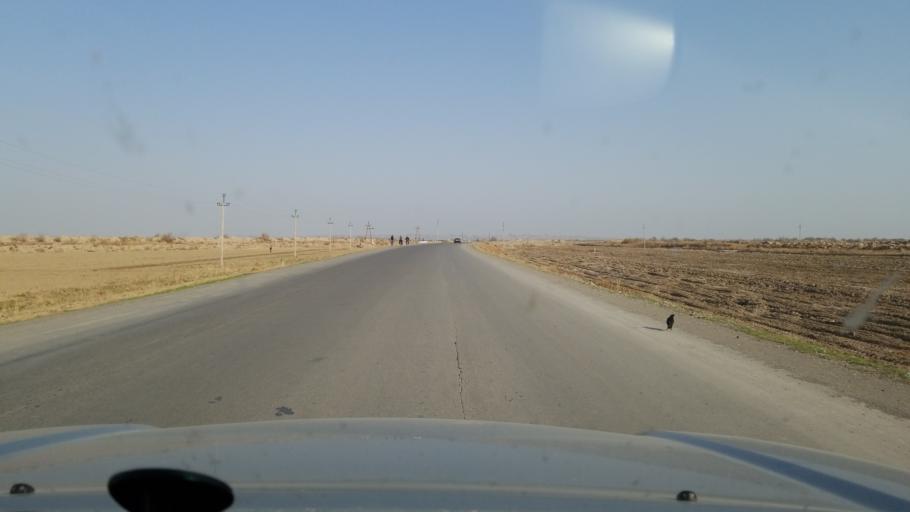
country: AF
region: Jowzjan
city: Khamyab
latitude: 37.5752
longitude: 65.8112
